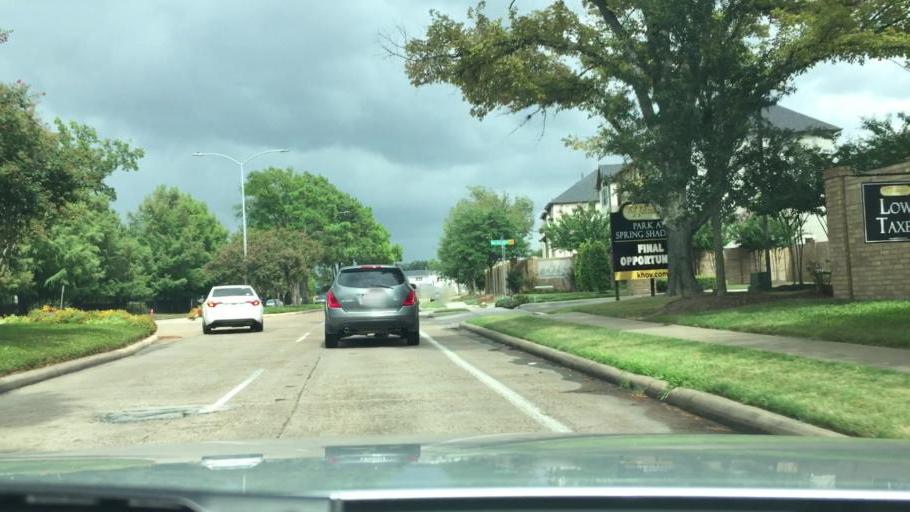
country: US
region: Texas
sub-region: Harris County
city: Spring Valley
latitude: 29.8217
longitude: -95.5383
